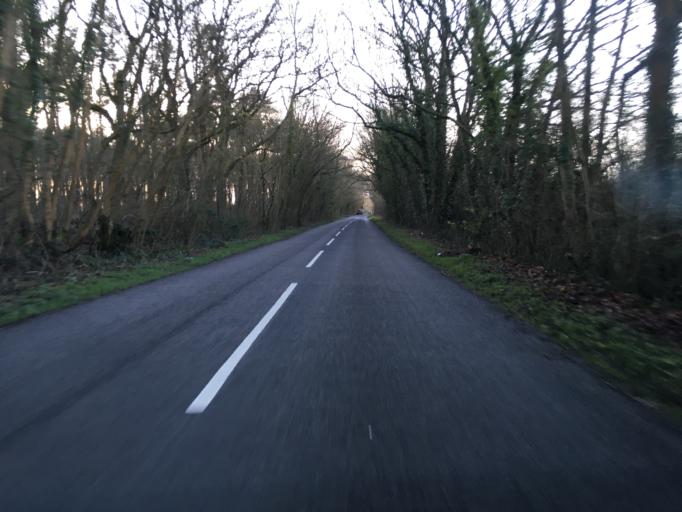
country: GB
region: England
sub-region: Warwickshire
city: Stratford-upon-Avon
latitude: 52.2278
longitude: -1.7246
